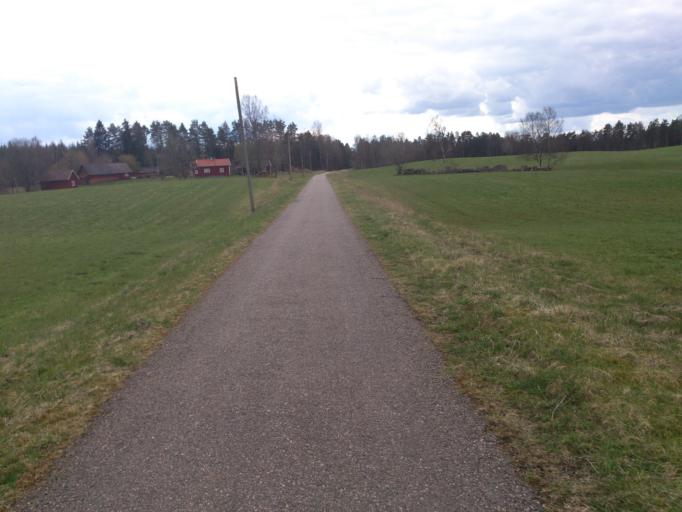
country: SE
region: Vaestra Goetaland
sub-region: Falkopings Kommun
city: Falkoeping
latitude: 57.9791
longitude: 13.5231
